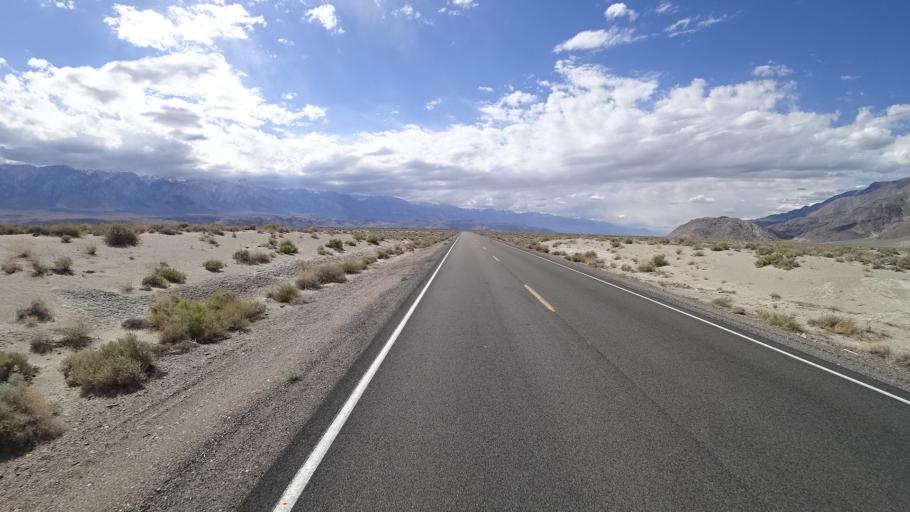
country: US
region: California
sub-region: Inyo County
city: Lone Pine
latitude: 36.5625
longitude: -117.9728
